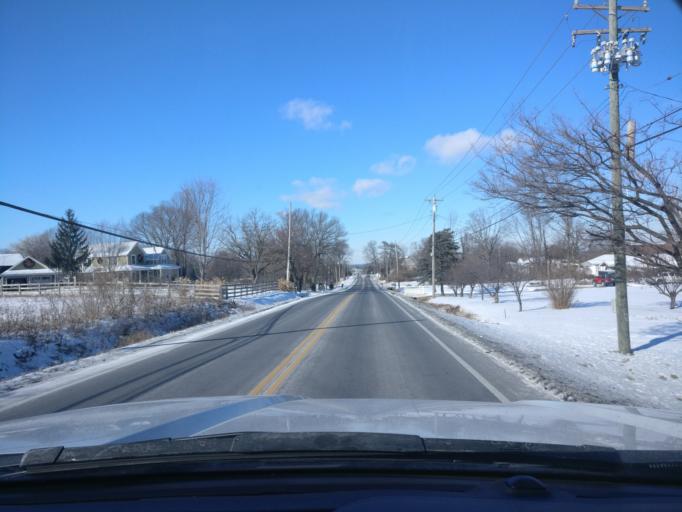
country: US
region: Ohio
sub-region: Warren County
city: Hunter
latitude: 39.5279
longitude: -84.2808
